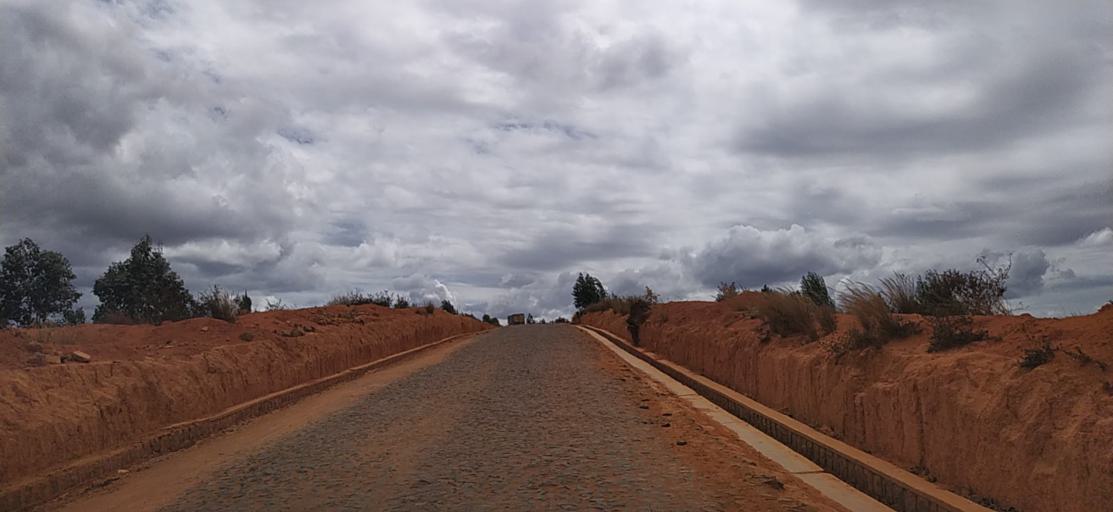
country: MG
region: Alaotra Mangoro
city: Ambatondrazaka
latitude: -18.0577
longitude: 48.2552
